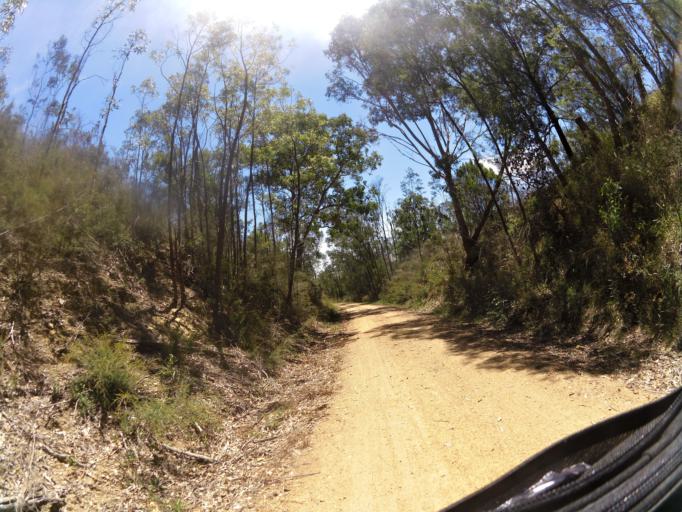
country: AU
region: Victoria
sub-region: East Gippsland
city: Lakes Entrance
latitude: -37.7314
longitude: 147.8607
